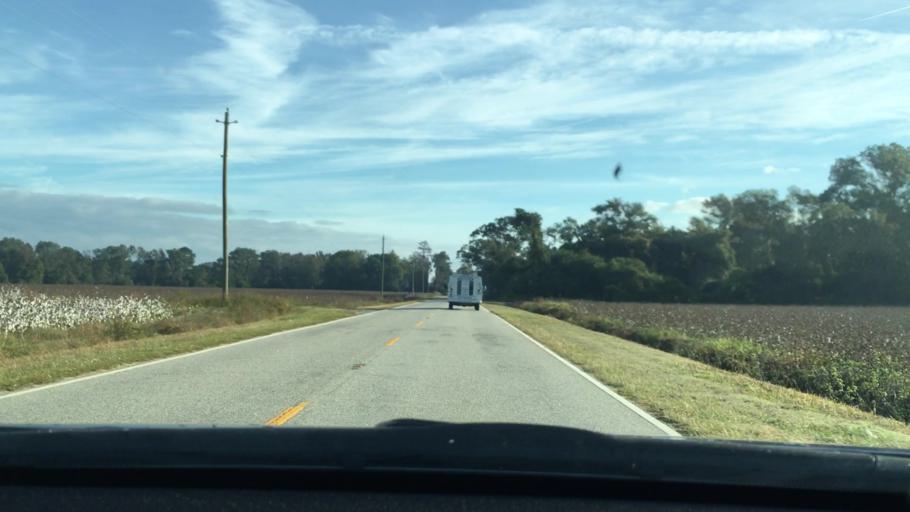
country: US
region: South Carolina
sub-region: Lee County
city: Bishopville
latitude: 34.0979
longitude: -80.1727
